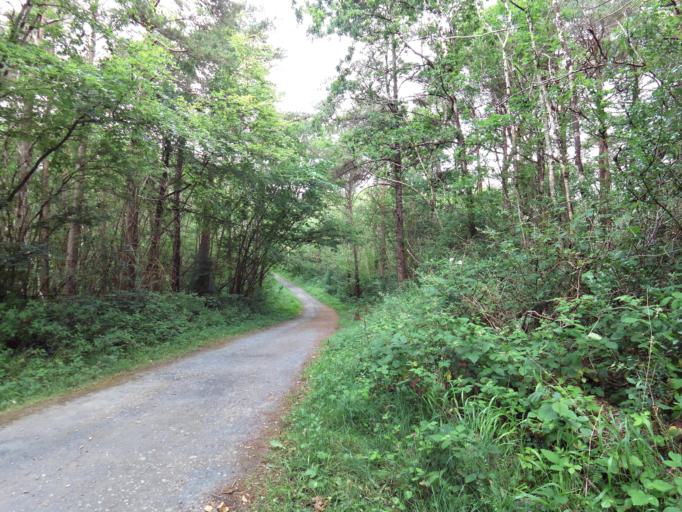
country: IE
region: Connaught
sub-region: County Galway
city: Gort
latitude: 53.0784
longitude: -8.8622
